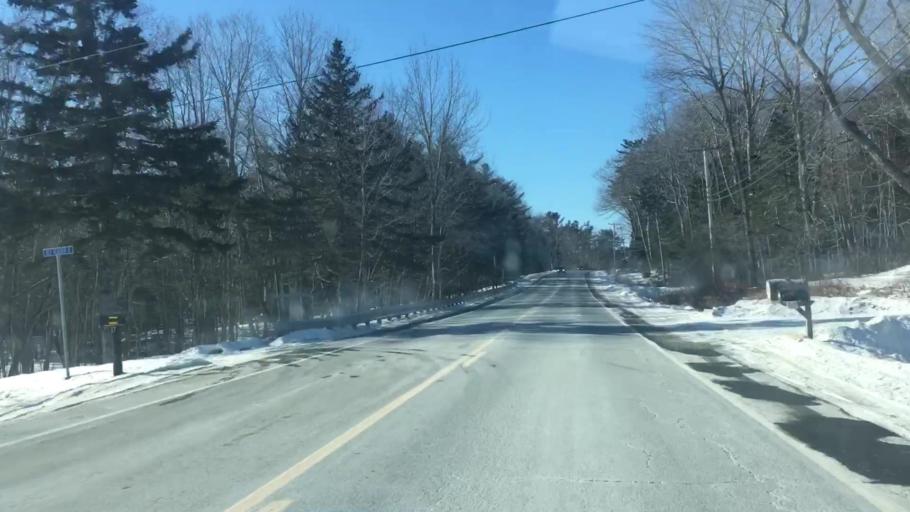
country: US
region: Maine
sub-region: Hancock County
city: Surry
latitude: 44.4948
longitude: -68.4730
